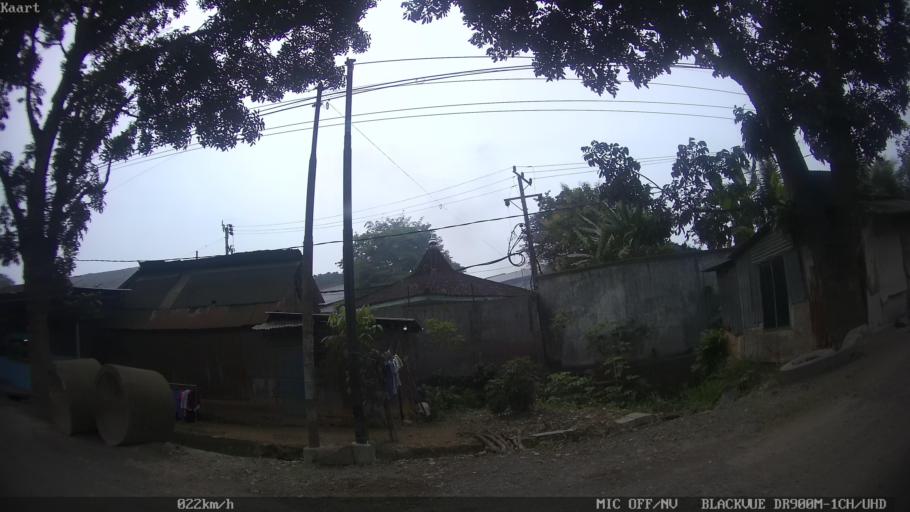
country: ID
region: Lampung
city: Panjang
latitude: -5.4242
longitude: 105.3311
